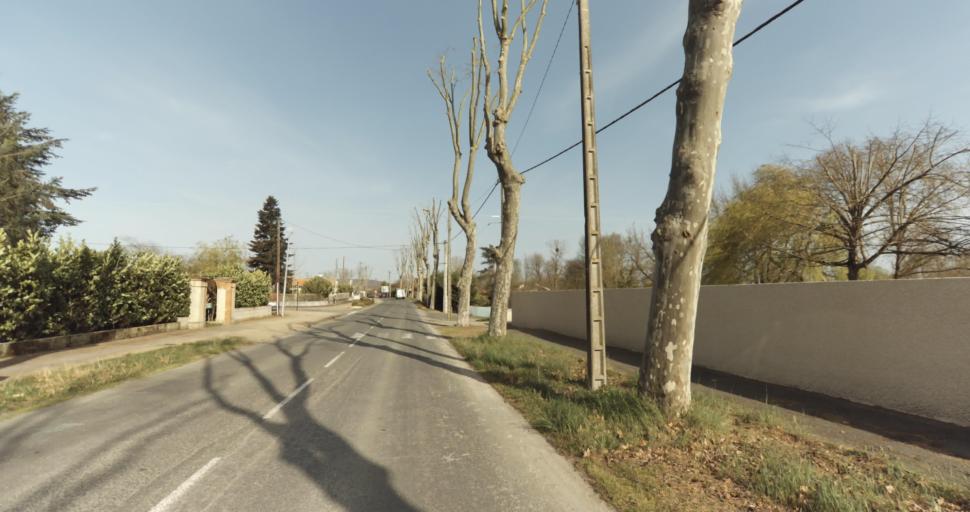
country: FR
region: Midi-Pyrenees
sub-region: Departement du Tarn
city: Saint-Sulpice-la-Pointe
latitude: 43.7656
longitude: 1.6939
